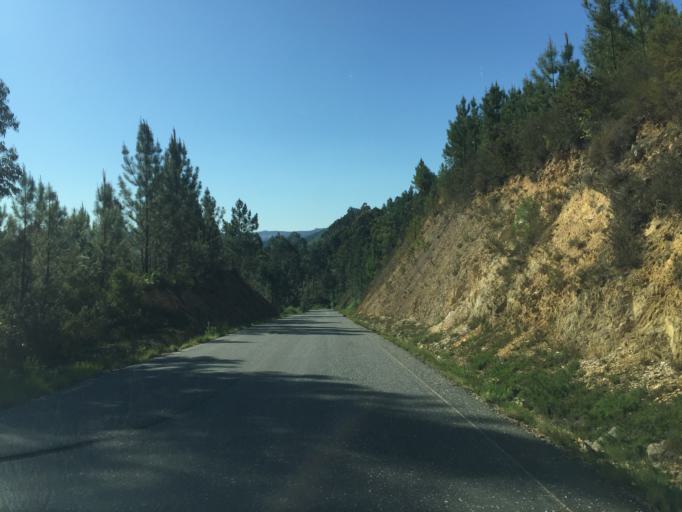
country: PT
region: Coimbra
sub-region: Pampilhosa da Serra
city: Pampilhosa da Serra
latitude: 40.0516
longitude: -7.8201
